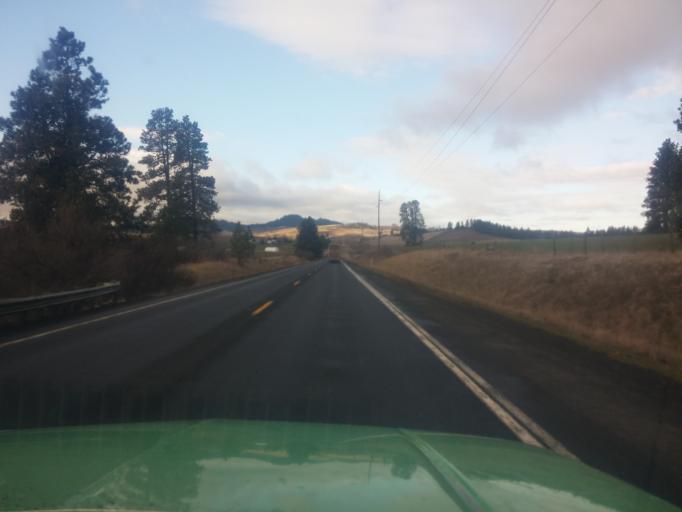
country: US
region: Idaho
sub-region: Latah County
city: Moscow
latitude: 46.9064
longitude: -116.9665
